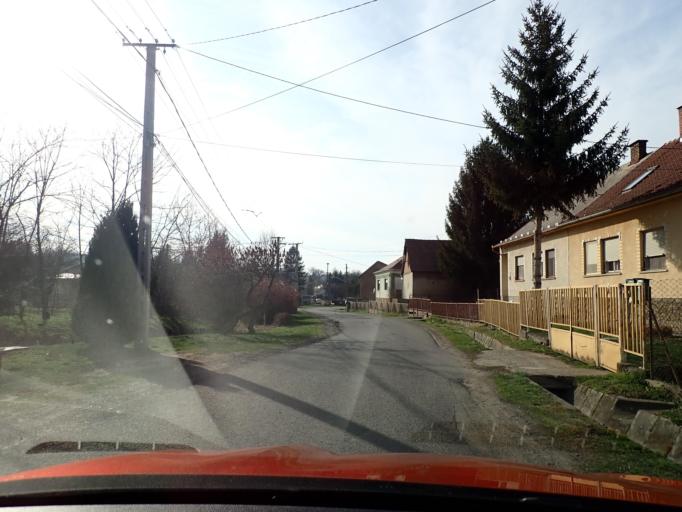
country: HU
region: Baranya
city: Komlo
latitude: 46.1614
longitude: 18.2467
